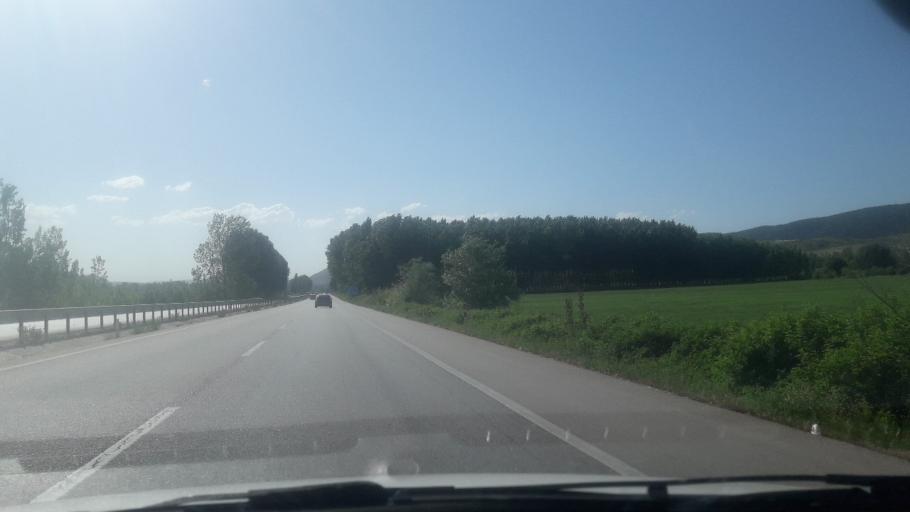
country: TR
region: Tokat
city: Dokmetepe
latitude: 40.3170
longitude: 36.2466
